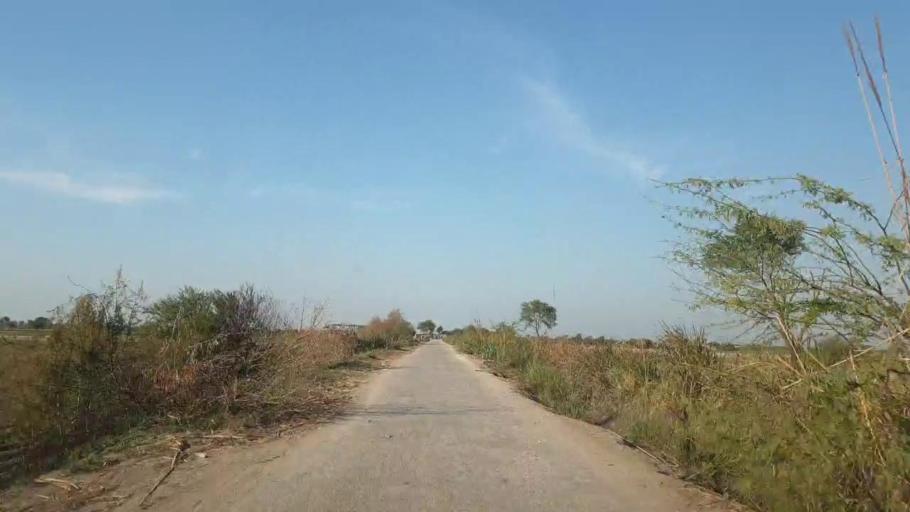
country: PK
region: Sindh
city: Tando Adam
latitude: 25.7275
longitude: 68.7026
